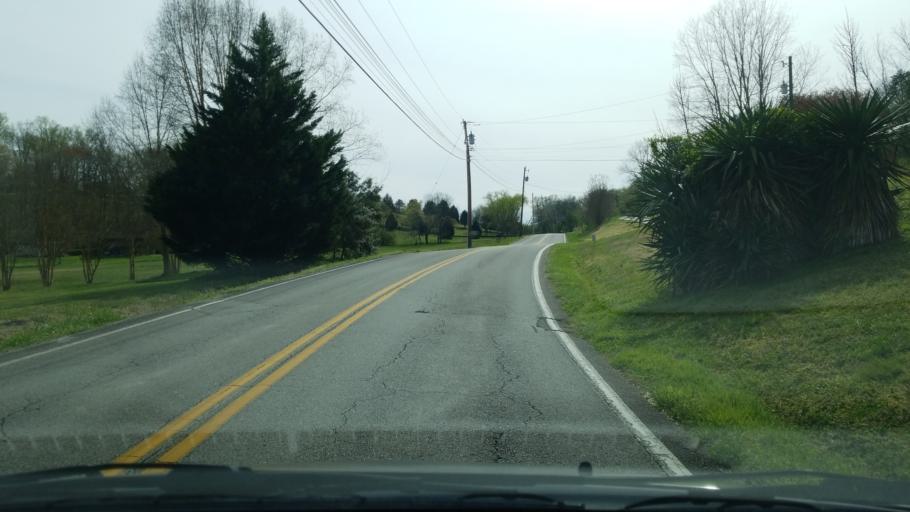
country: US
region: Tennessee
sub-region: Hamilton County
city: Falling Water
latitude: 35.1783
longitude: -85.2563
